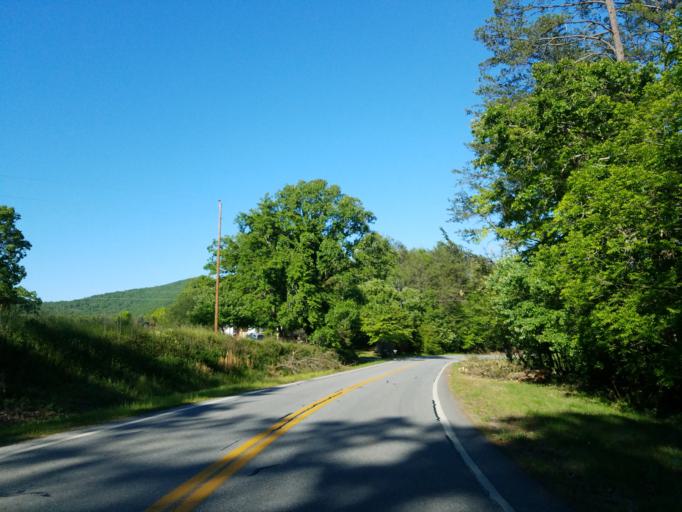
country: US
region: Georgia
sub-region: Fannin County
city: Blue Ridge
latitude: 34.8456
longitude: -84.2044
